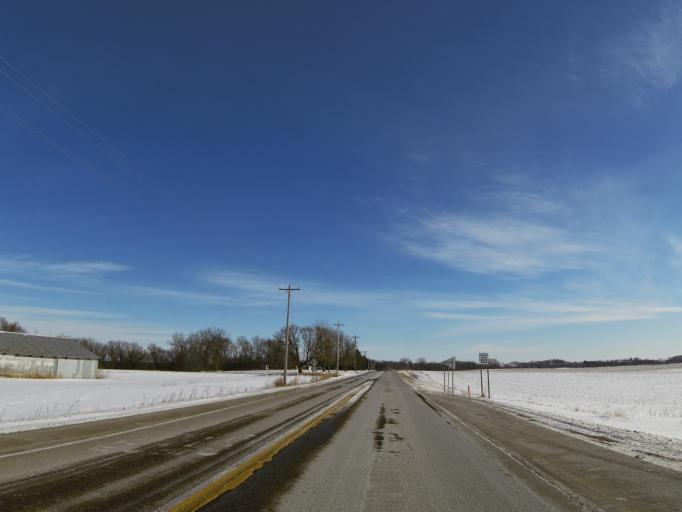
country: US
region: Minnesota
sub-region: Washington County
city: Cottage Grove
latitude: 44.7424
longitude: -92.9483
